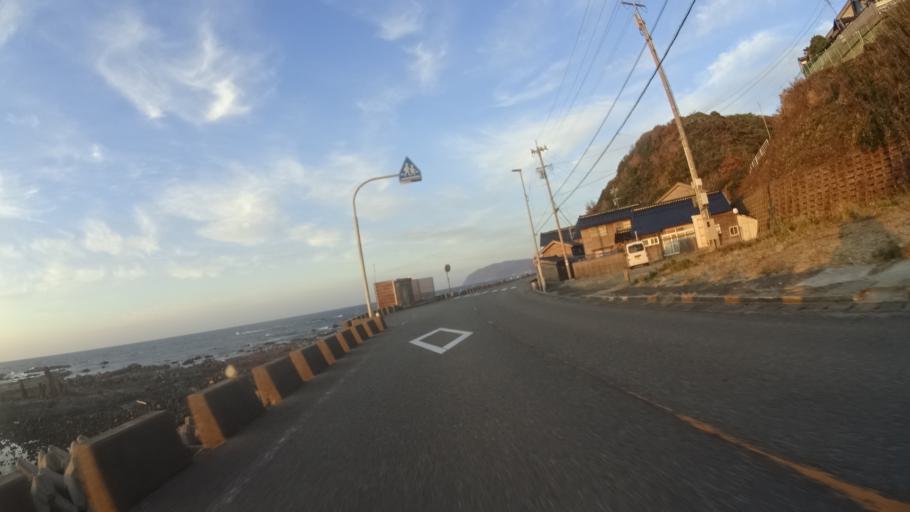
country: JP
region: Ishikawa
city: Nanao
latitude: 37.2412
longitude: 136.7014
